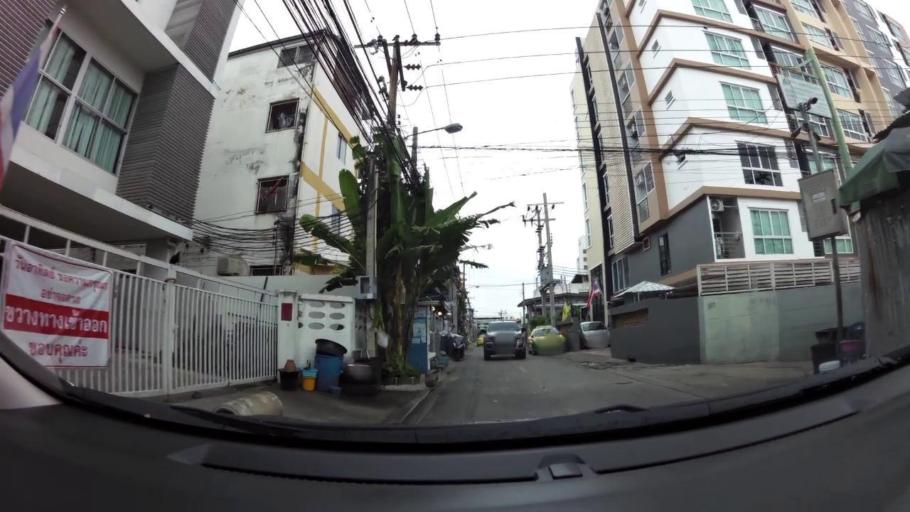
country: TH
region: Bangkok
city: Phra Khanong
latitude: 13.7072
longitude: 100.6143
